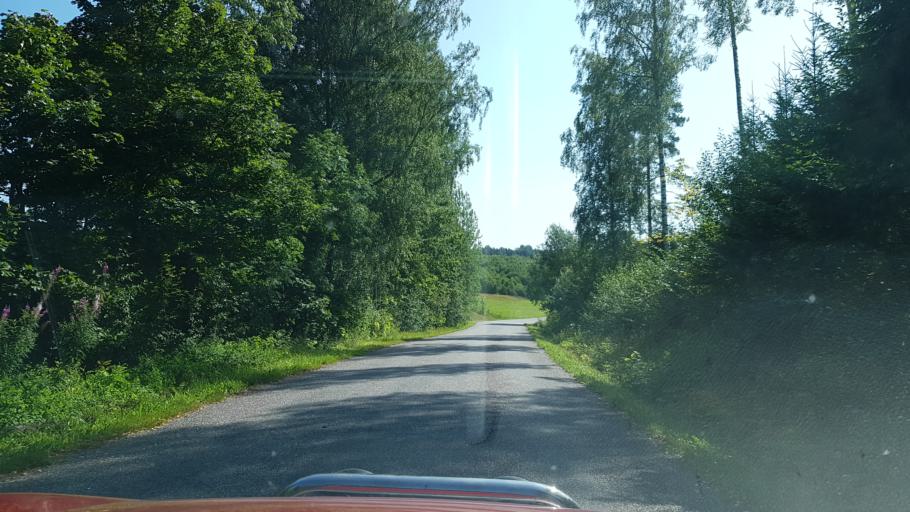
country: EE
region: Vorumaa
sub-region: Voru linn
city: Voru
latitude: 57.7202
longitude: 27.1050
